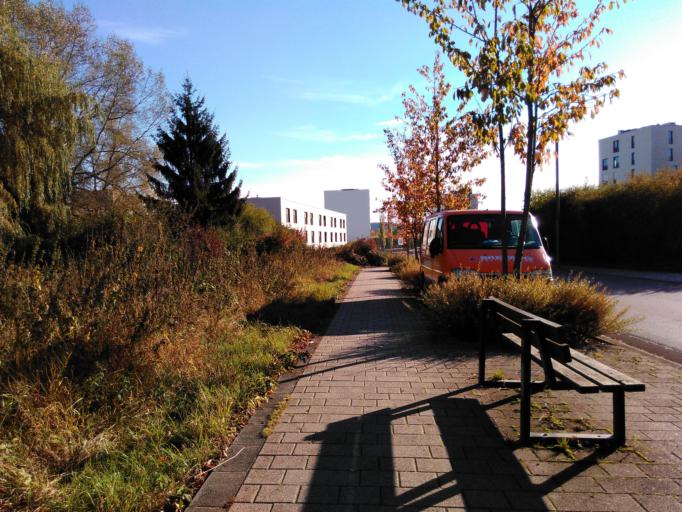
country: LU
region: Luxembourg
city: Belvaux
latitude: 49.5098
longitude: 5.9382
